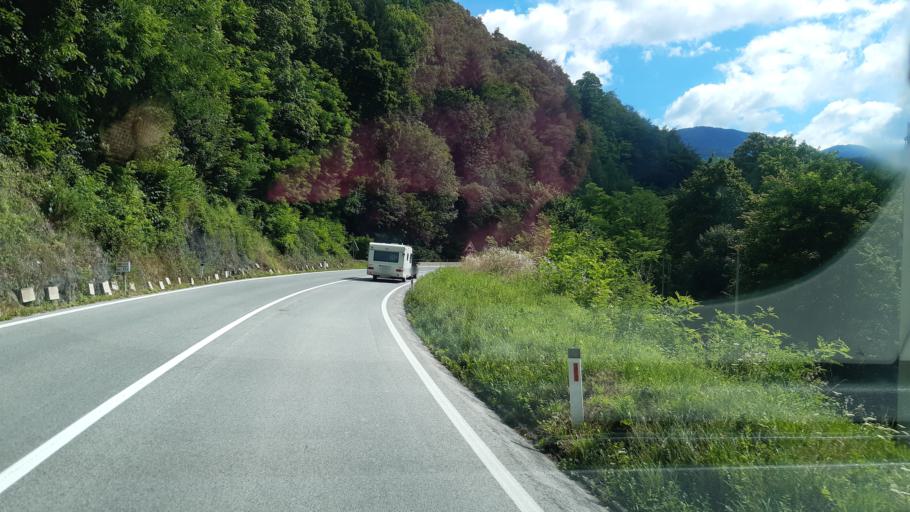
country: SI
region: Trzic
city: Trzic
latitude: 46.3617
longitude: 14.3018
